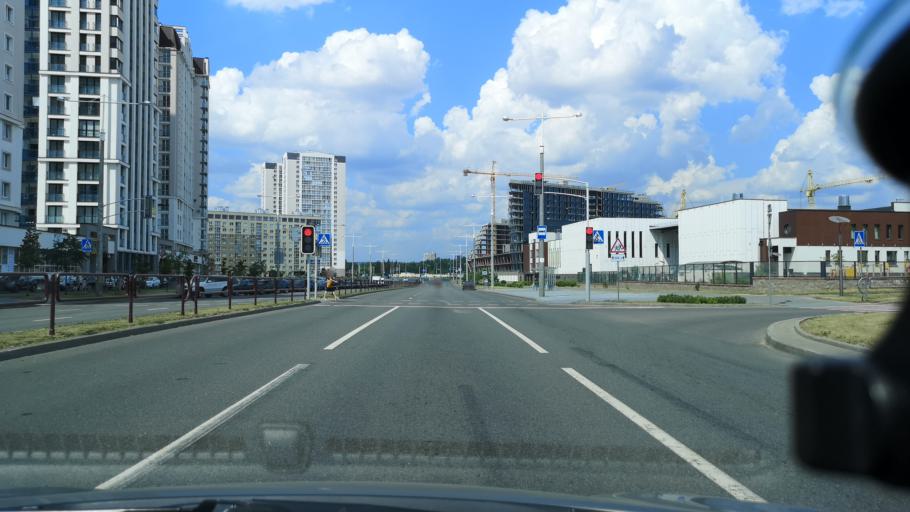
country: BY
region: Minsk
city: Borovlyany
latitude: 53.9302
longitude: 27.6559
